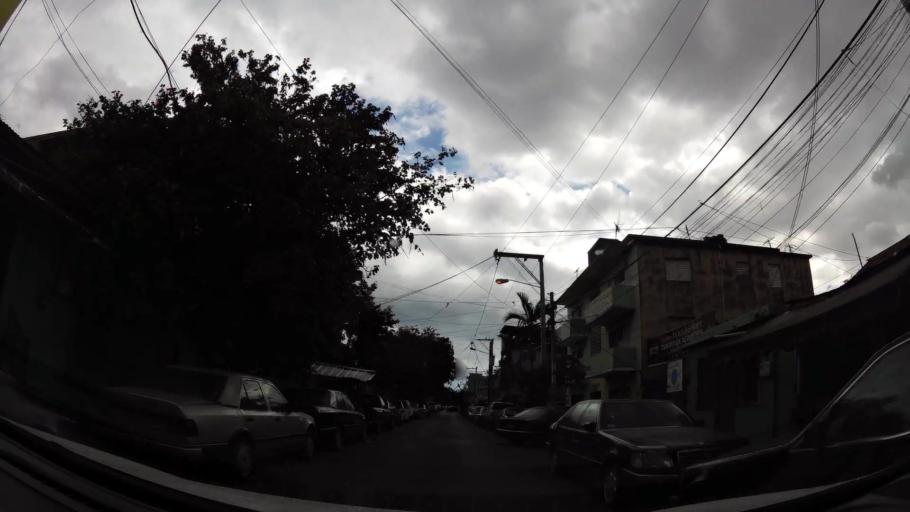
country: DO
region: Nacional
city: San Carlos
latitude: 18.4894
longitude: -69.9110
